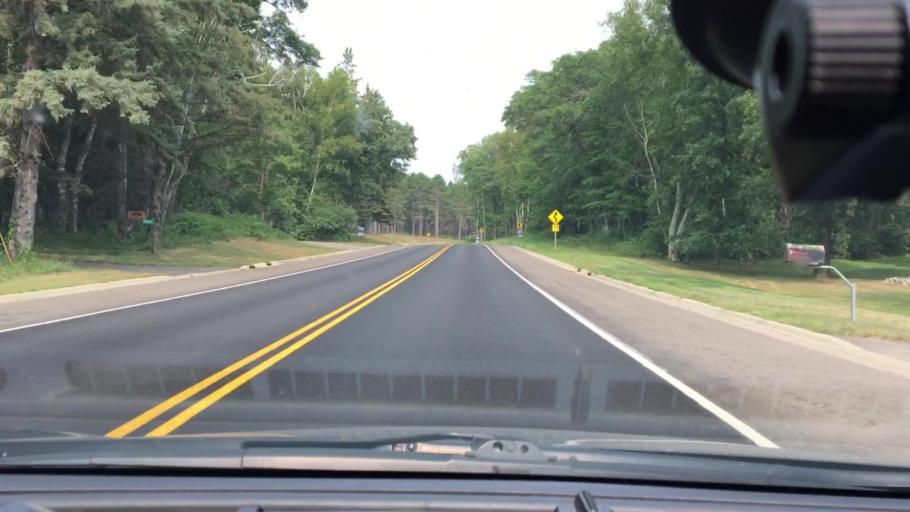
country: US
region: Minnesota
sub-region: Crow Wing County
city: Cross Lake
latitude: 46.7025
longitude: -94.0604
